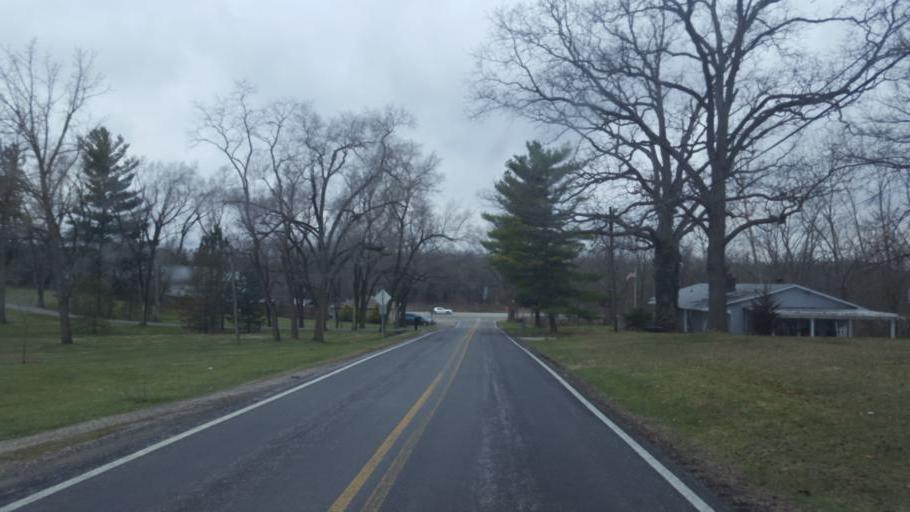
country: US
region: Ohio
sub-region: Delaware County
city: Delaware
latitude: 40.3559
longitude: -83.0721
